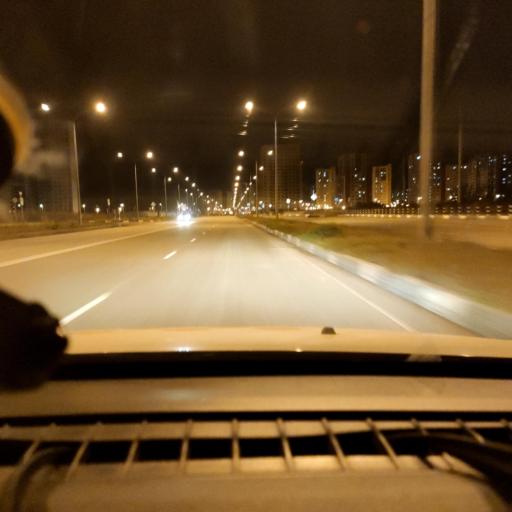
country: RU
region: Samara
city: Samara
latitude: 53.1420
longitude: 50.0778
